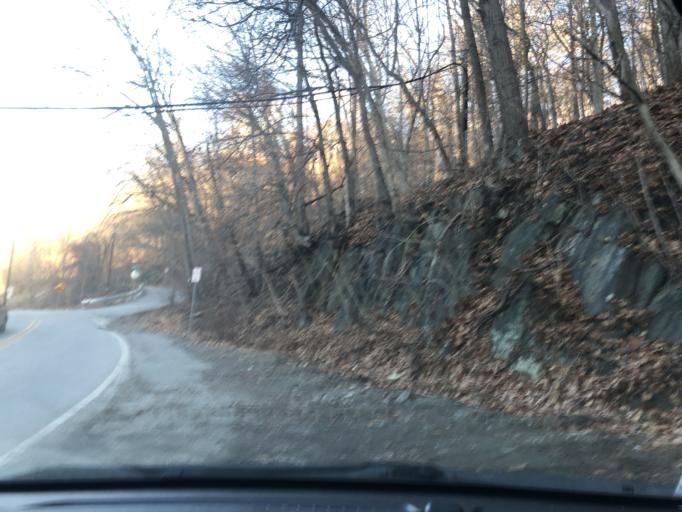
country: US
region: Maryland
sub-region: Howard County
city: Ilchester
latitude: 39.2517
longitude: -76.7636
